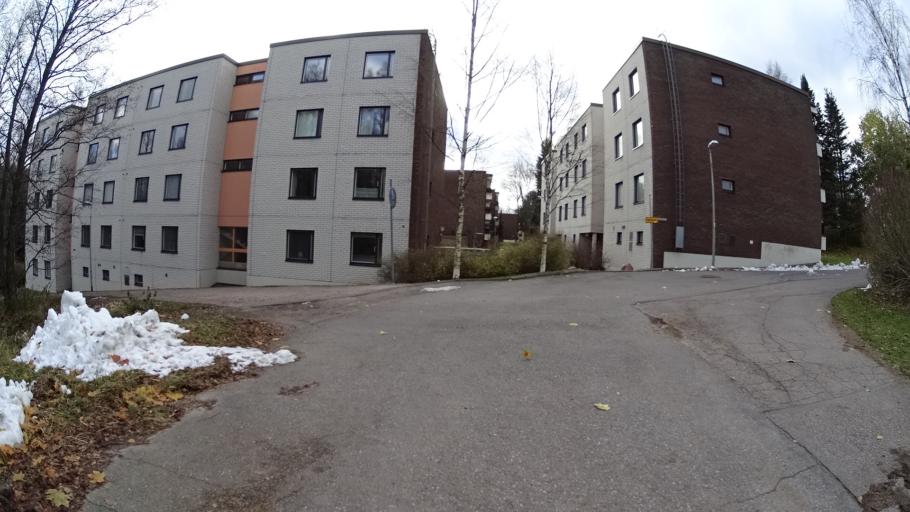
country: FI
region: Uusimaa
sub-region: Helsinki
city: Teekkarikylae
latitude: 60.2617
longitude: 24.8599
